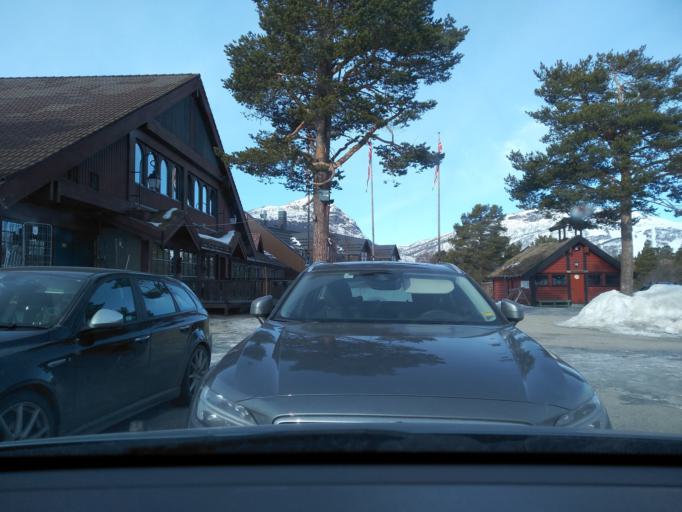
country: NO
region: Aust-Agder
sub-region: Bykle
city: Hovden
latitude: 59.5553
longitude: 7.3597
